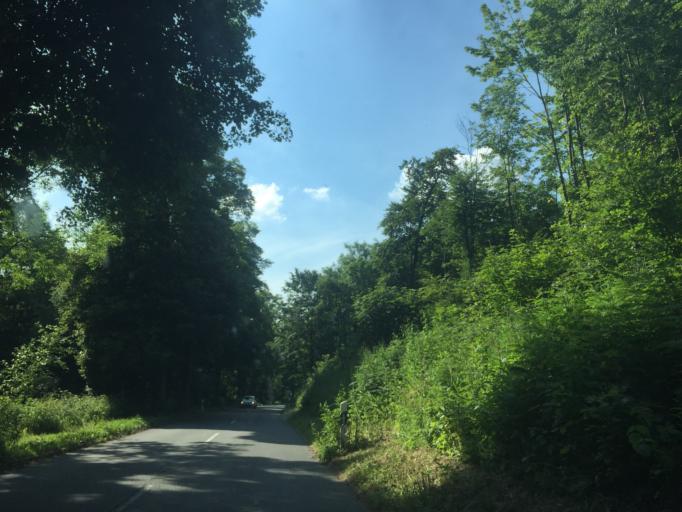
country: DE
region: Baden-Wuerttemberg
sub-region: Karlsruhe Region
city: Gaiberg
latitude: 49.3807
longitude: 8.7222
